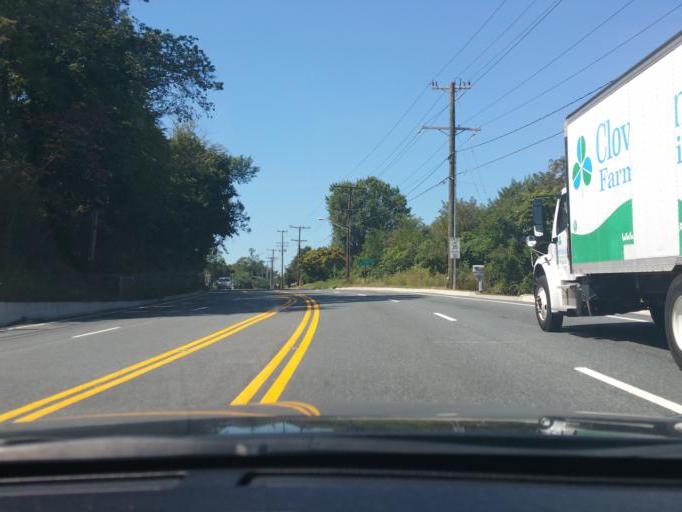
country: US
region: Maryland
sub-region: Harford County
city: Havre de Grace
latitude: 39.5618
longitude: -76.1094
